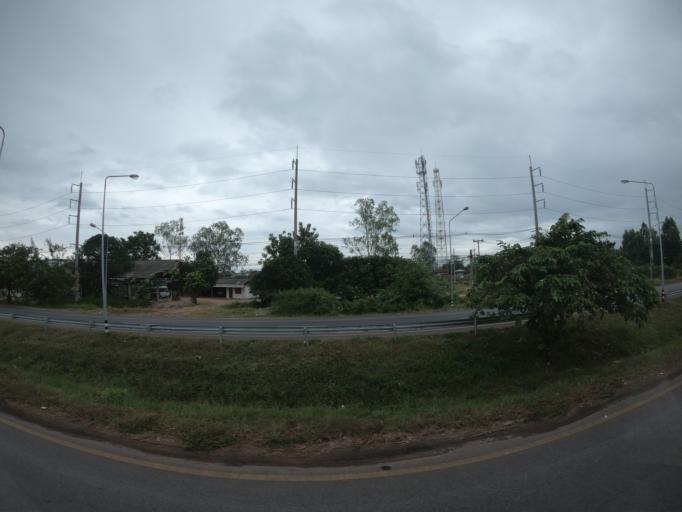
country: TH
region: Roi Et
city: Roi Et
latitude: 16.0479
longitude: 103.6217
